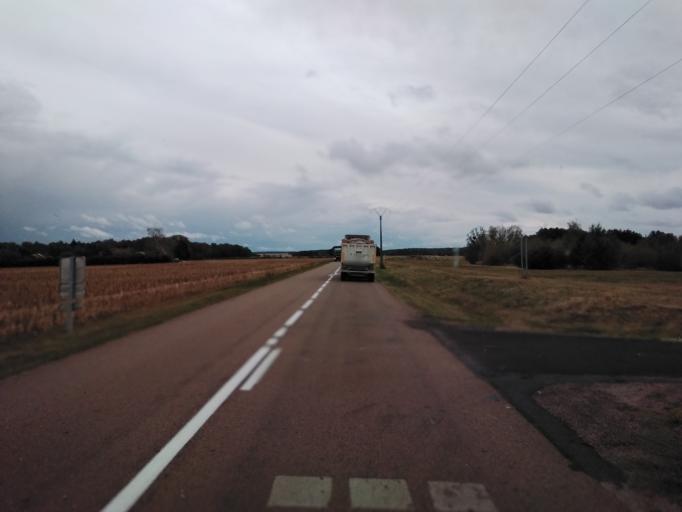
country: FR
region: Champagne-Ardenne
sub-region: Departement de l'Aube
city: Brienne-le-Chateau
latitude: 48.3451
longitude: 4.5289
